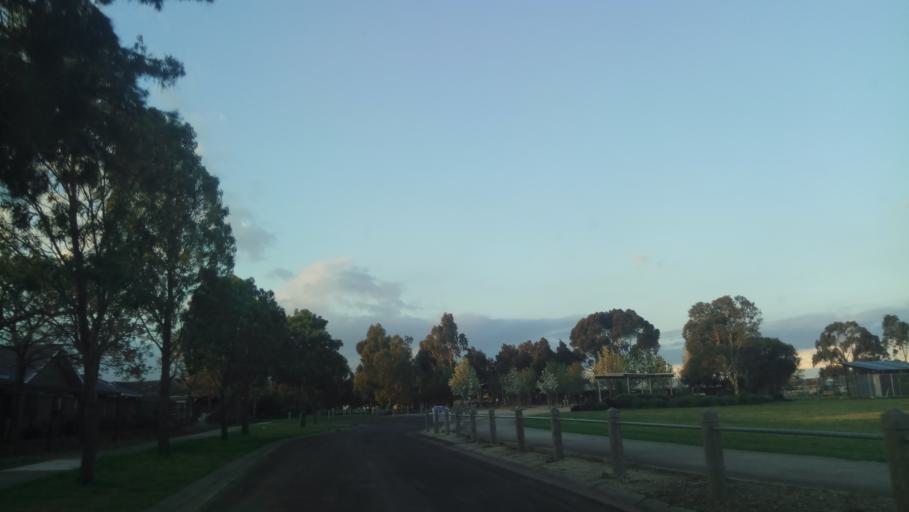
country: AU
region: Victoria
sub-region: Hobsons Bay
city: Altona Meadows
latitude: -37.8792
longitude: 144.7822
